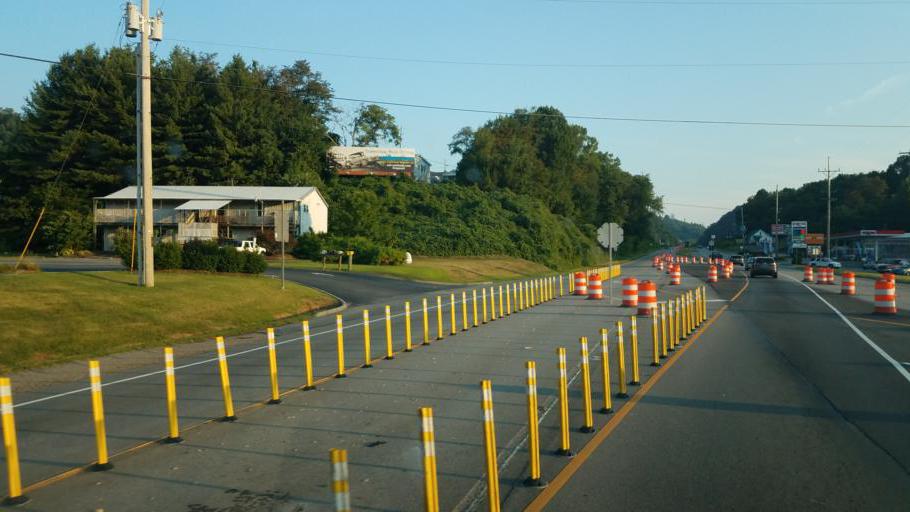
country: US
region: Virginia
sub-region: Scott County
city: Weber City
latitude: 36.6078
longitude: -82.5690
